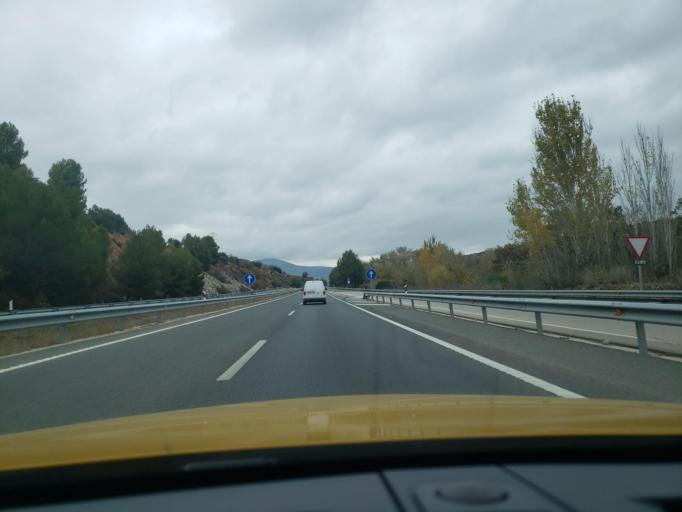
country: ES
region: Andalusia
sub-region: Provincia de Granada
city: Deifontes
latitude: 37.3462
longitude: -3.6183
